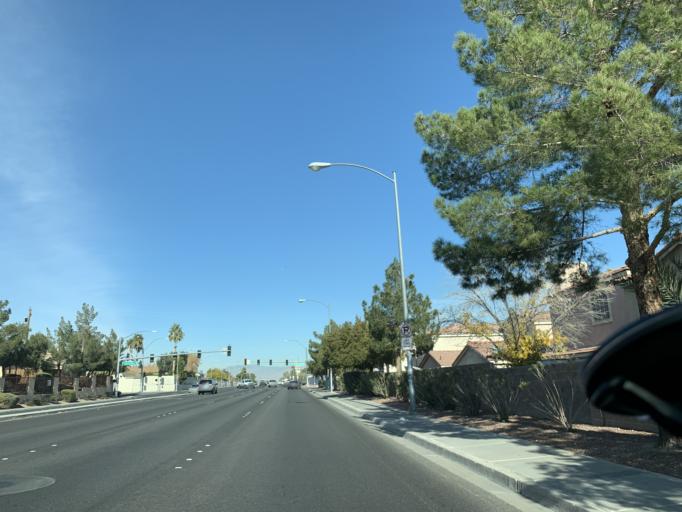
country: US
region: Nevada
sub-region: Clark County
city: Spring Valley
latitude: 36.0916
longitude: -115.2250
